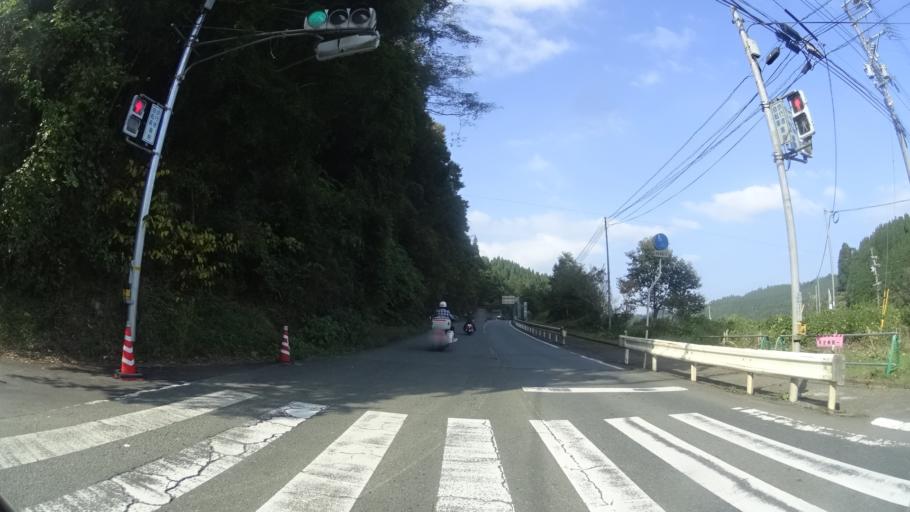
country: JP
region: Kumamoto
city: Aso
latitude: 33.0928
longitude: 131.0665
